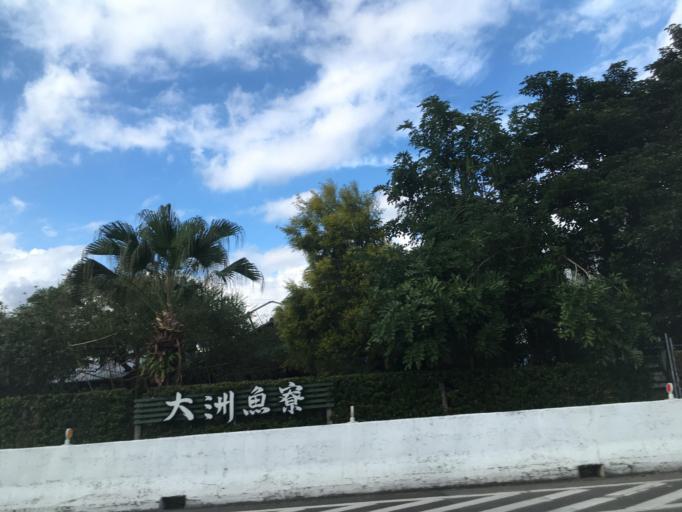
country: TW
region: Taiwan
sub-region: Yilan
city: Yilan
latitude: 24.6876
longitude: 121.7195
